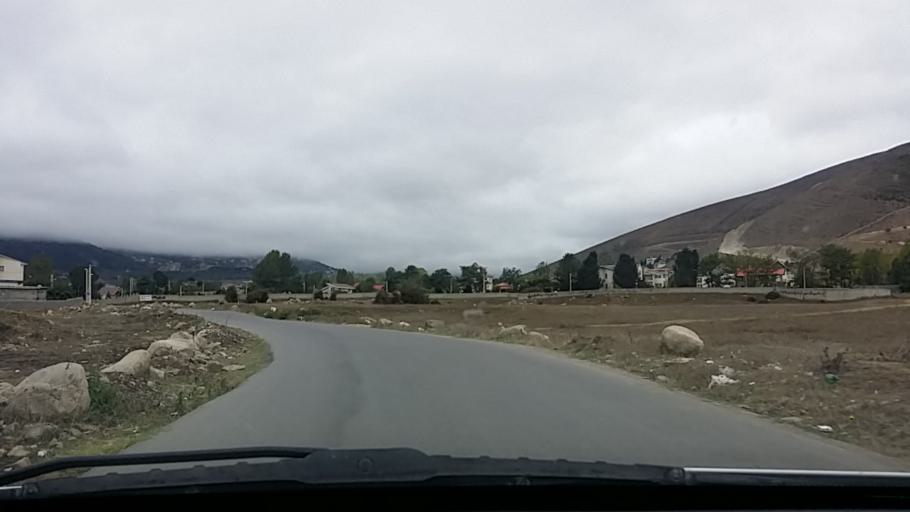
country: IR
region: Mazandaran
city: `Abbasabad
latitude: 36.5184
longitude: 51.1689
